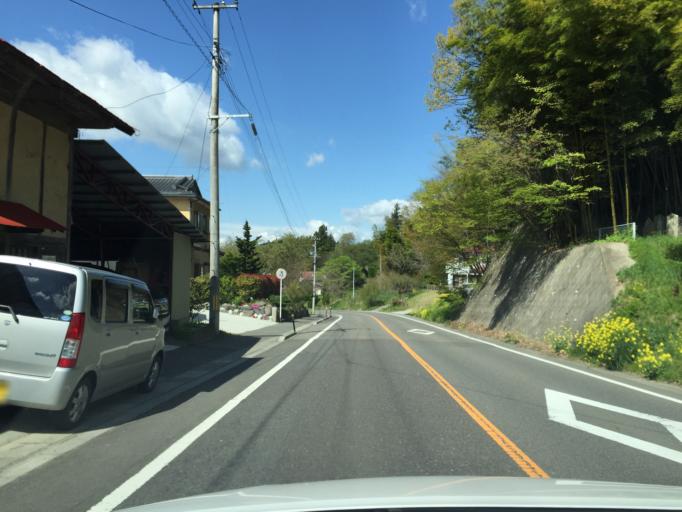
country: JP
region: Fukushima
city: Funehikimachi-funehiki
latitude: 37.5401
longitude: 140.5704
